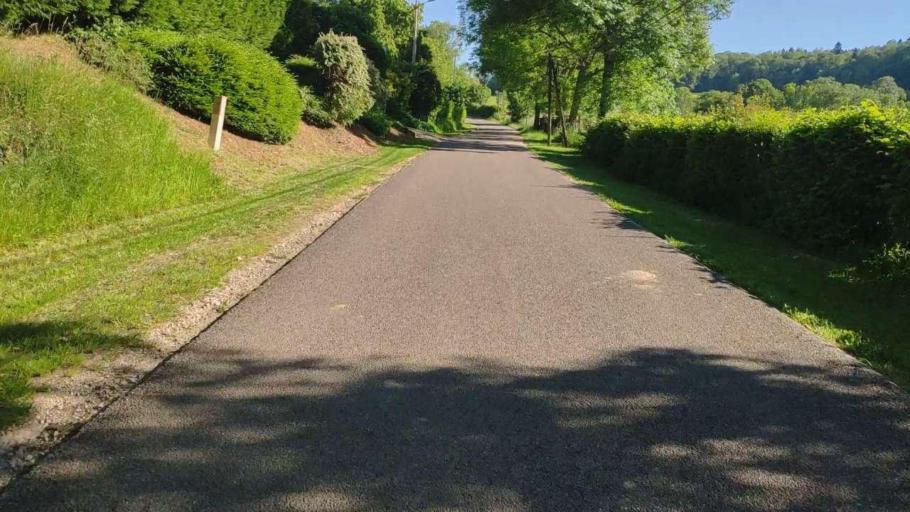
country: FR
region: Franche-Comte
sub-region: Departement du Jura
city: Lons-le-Saunier
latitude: 46.7240
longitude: 5.5544
